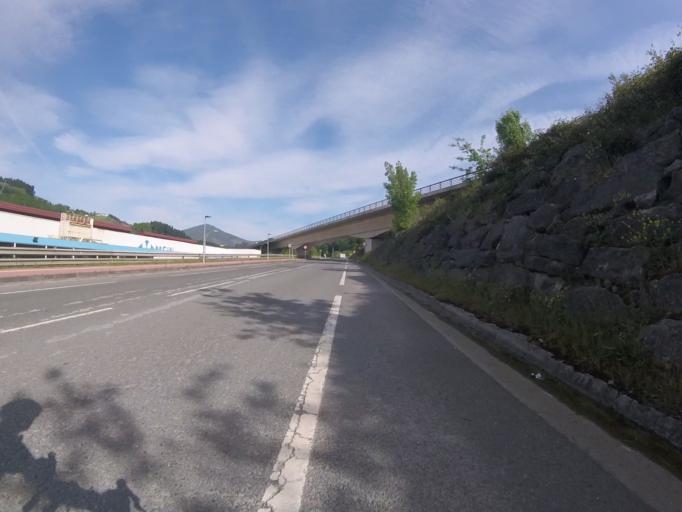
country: ES
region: Basque Country
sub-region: Provincia de Guipuzcoa
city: Gabiria
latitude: 43.0732
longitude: -2.2885
